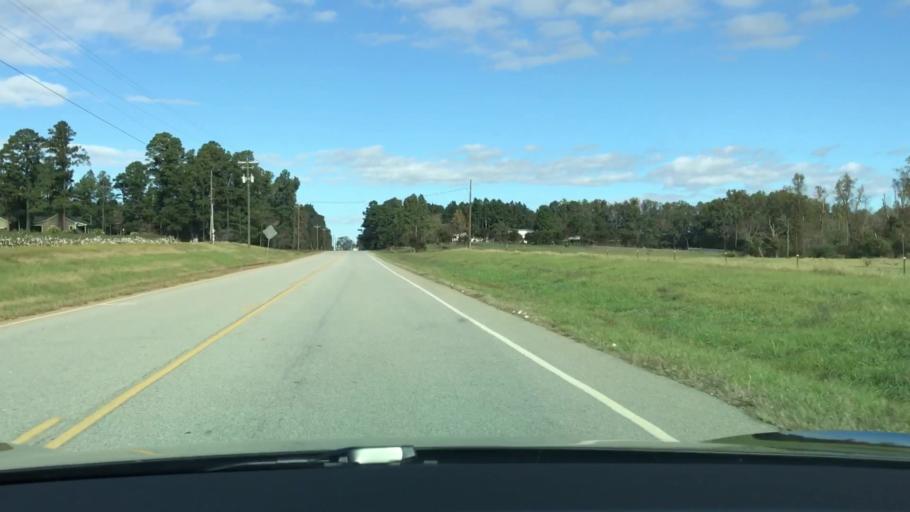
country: US
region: Georgia
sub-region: Jefferson County
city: Wrens
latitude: 33.1325
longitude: -82.4531
